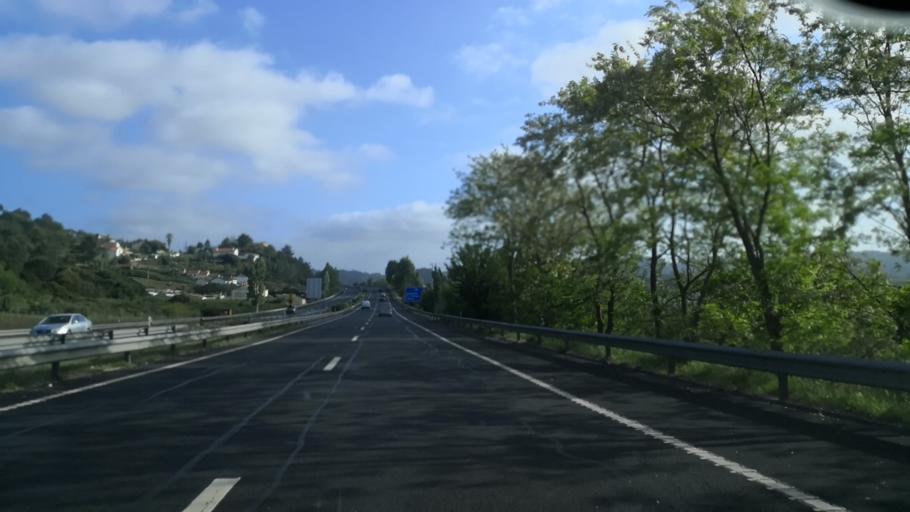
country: PT
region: Leiria
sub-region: Obidos
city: Obidos
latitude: 39.3281
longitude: -9.1754
